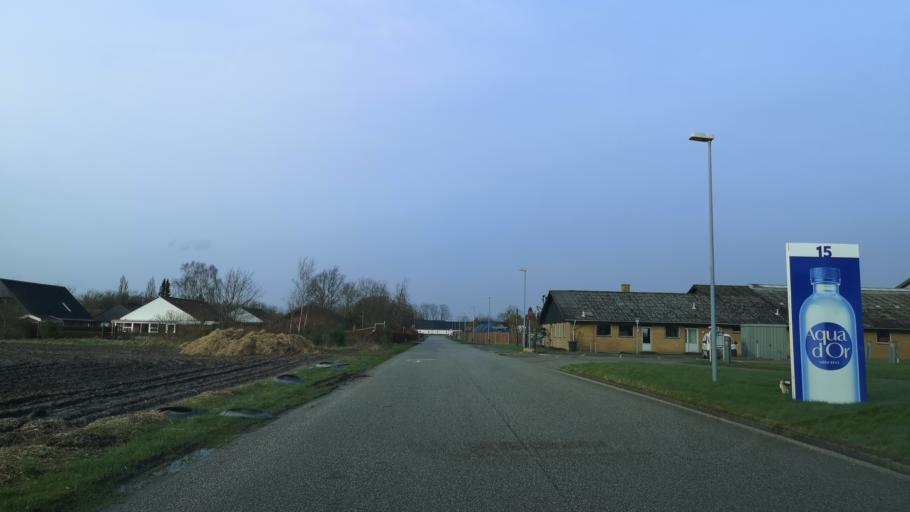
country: DK
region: Central Jutland
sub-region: Ikast-Brande Kommune
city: Brande
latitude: 56.0050
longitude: 9.1155
